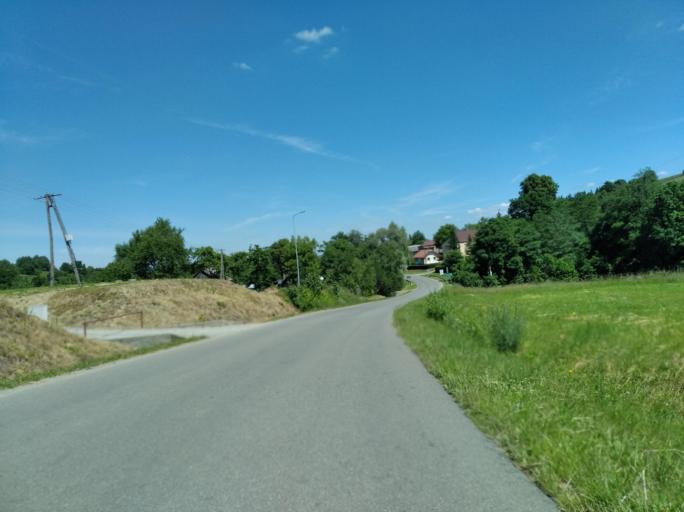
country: PL
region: Subcarpathian Voivodeship
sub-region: Powiat jasielski
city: Tarnowiec
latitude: 49.6848
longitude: 21.5446
